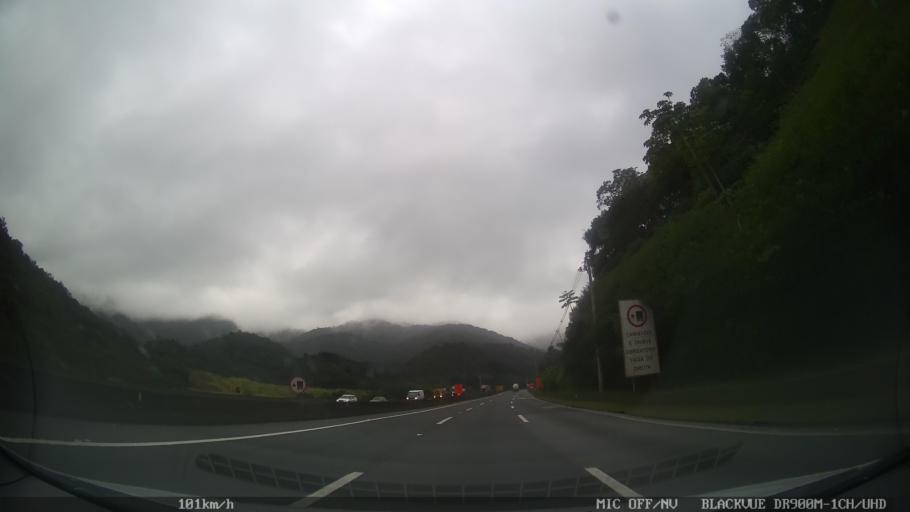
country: BR
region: Sao Paulo
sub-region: Juquitiba
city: Juquitiba
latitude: -24.0787
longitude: -47.2513
